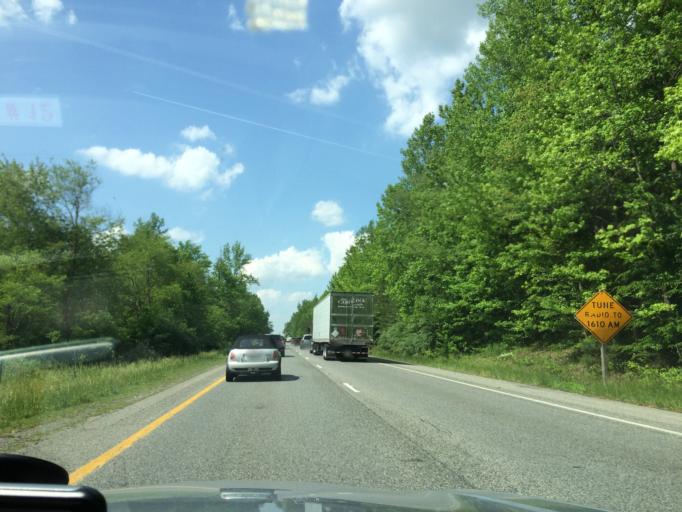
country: US
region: Maryland
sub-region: Prince George's County
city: Bowie
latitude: 38.9295
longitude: -76.7168
